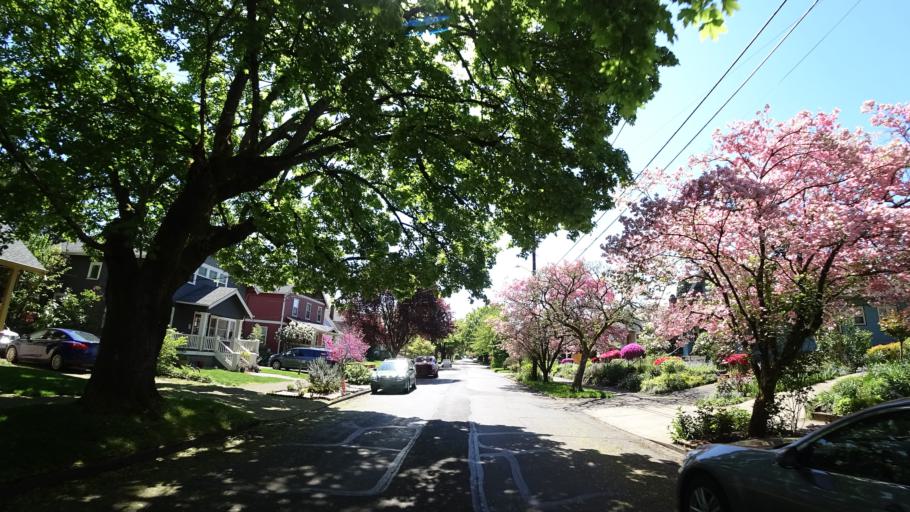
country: US
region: Oregon
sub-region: Clackamas County
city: Milwaukie
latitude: 45.4711
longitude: -122.6455
